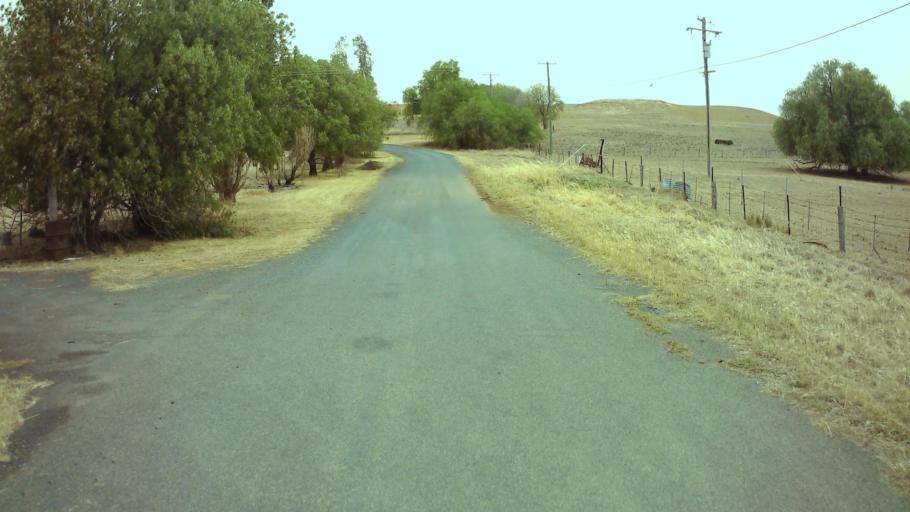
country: AU
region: New South Wales
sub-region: Weddin
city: Grenfell
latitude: -33.9062
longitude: 148.1699
